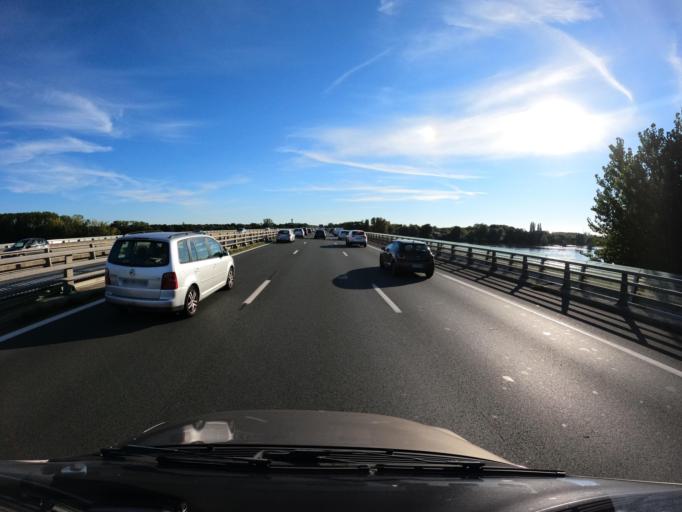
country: FR
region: Pays de la Loire
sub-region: Departement de Maine-et-Loire
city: Les Ponts-de-Ce
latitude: 47.4202
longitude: -0.5043
